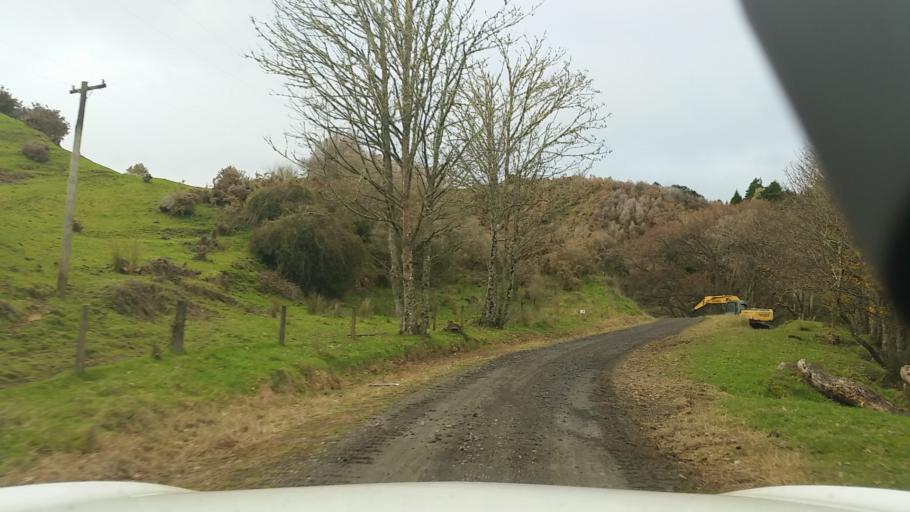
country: NZ
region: Taranaki
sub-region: New Plymouth District
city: Waitara
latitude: -39.1523
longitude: 174.5219
